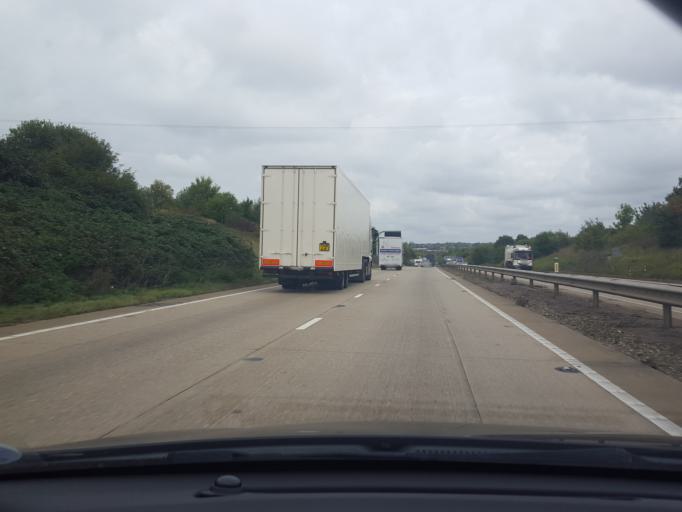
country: GB
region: England
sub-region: Suffolk
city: Bramford
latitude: 52.0528
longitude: 1.1002
